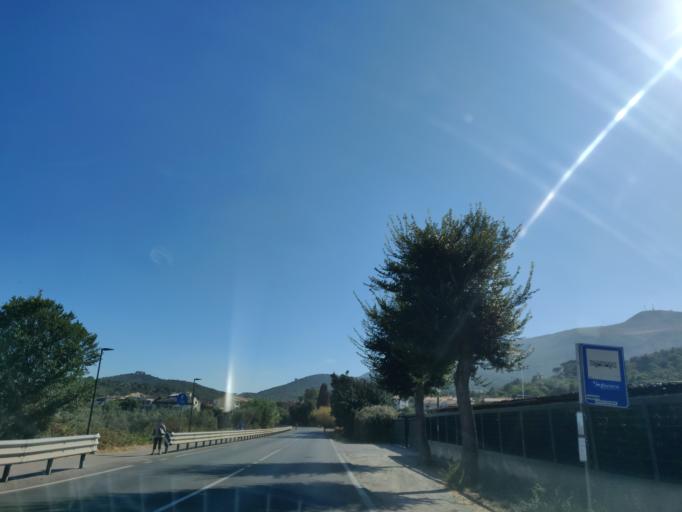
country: IT
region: Tuscany
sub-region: Provincia di Grosseto
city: Porto Ercole
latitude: 42.4034
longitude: 11.2000
